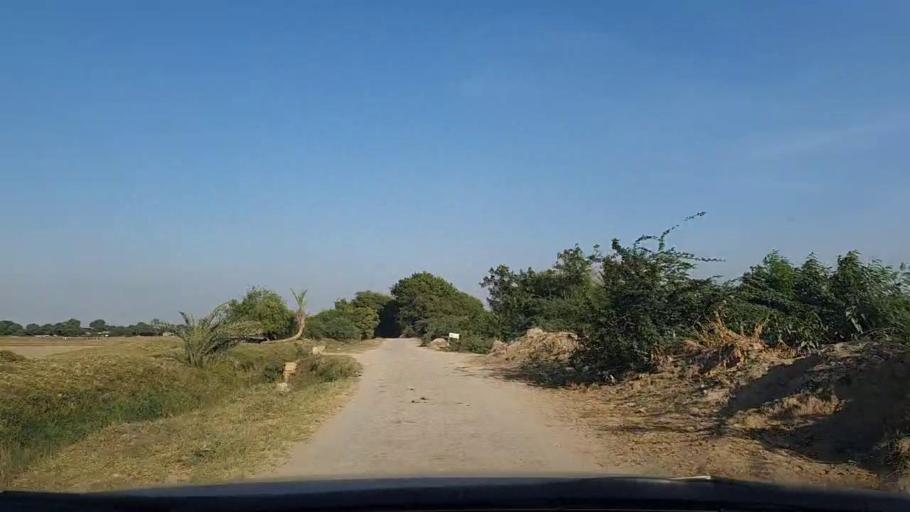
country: PK
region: Sindh
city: Mirpur Sakro
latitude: 24.5265
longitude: 67.6476
